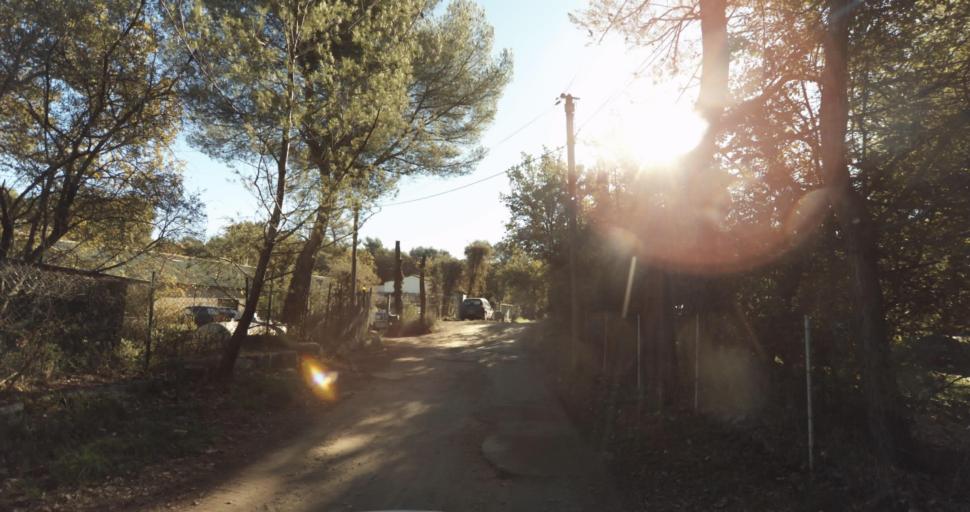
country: FR
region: Provence-Alpes-Cote d'Azur
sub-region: Departement des Alpes-Maritimes
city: La Colle-sur-Loup
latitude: 43.7101
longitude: 7.0855
